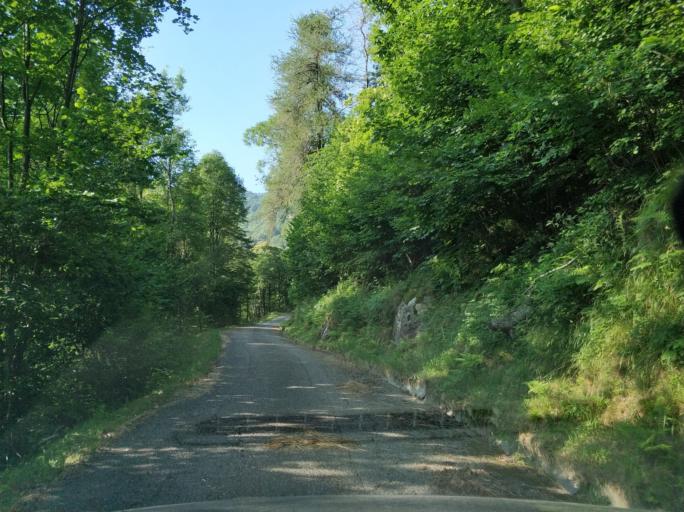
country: IT
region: Piedmont
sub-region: Provincia di Torino
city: Ceres
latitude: 45.3121
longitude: 7.3682
